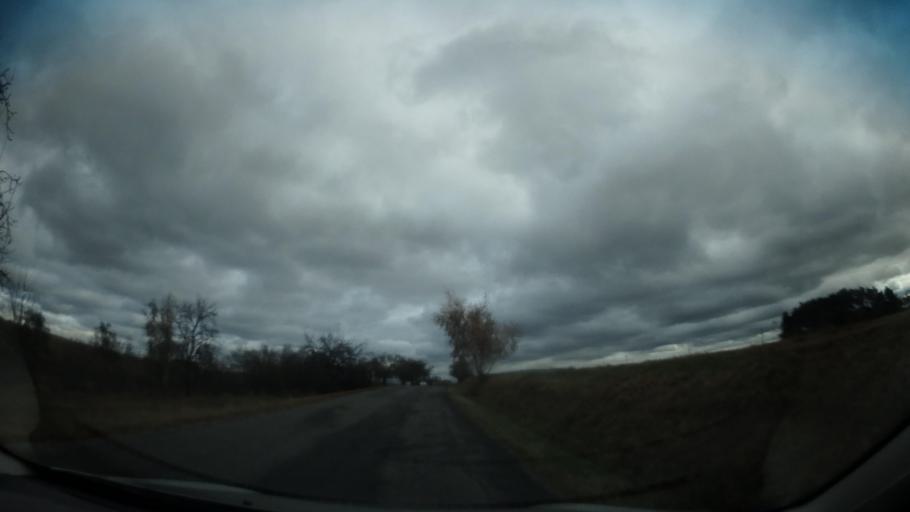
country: CZ
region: Vysocina
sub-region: Okres Zd'ar nad Sazavou
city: Velka Bites
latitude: 49.2909
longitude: 16.1461
